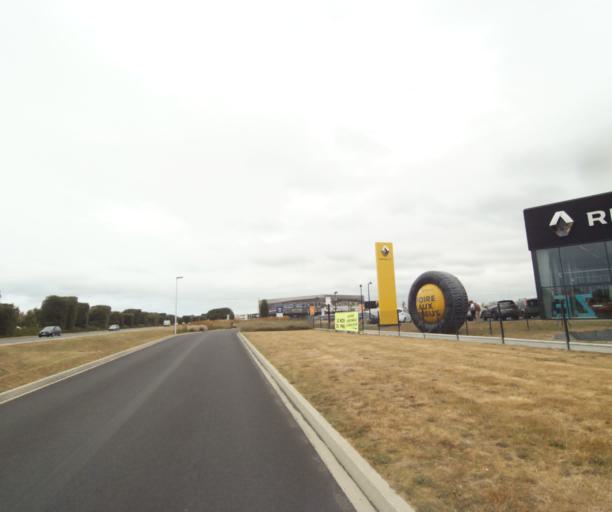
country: FR
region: Pays de la Loire
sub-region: Departement de la Vendee
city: Chateau-d'Olonne
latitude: 46.4964
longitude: -1.7529
